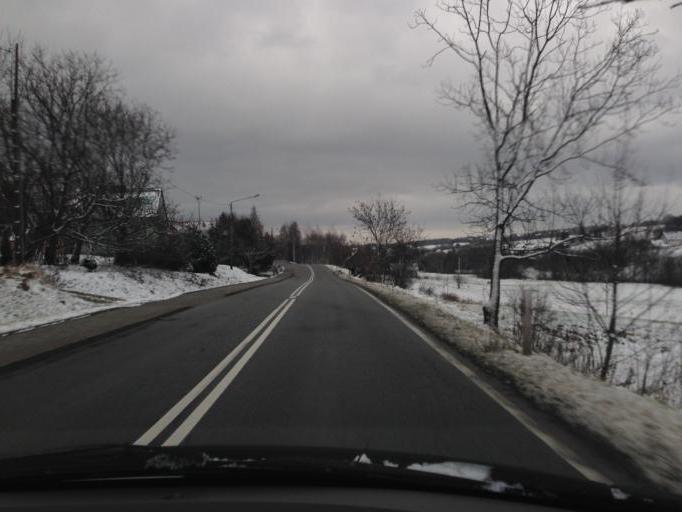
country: PL
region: Lesser Poland Voivodeship
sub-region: Powiat tarnowski
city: Siemiechow
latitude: 49.8530
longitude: 20.9066
